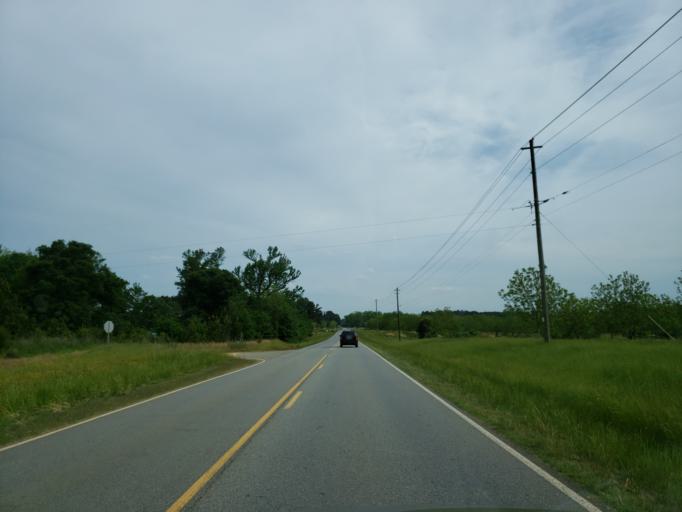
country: US
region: Georgia
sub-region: Dooly County
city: Vienna
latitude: 32.1597
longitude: -83.8837
